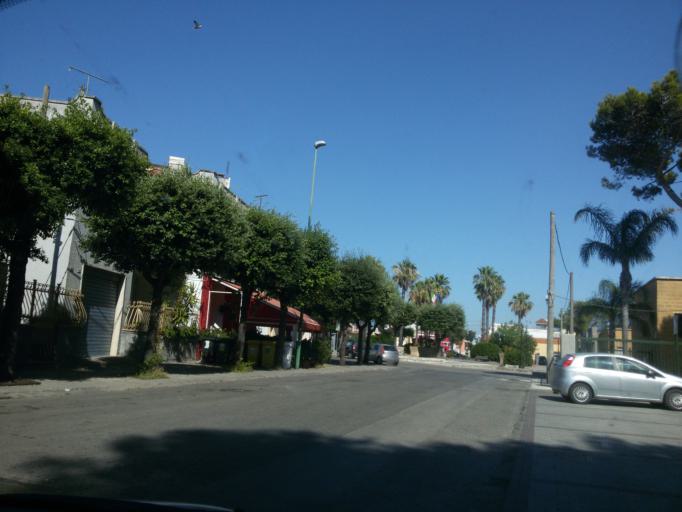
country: IT
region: Apulia
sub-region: Provincia di Brindisi
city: San Pancrazio Salentino
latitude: 40.4169
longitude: 17.8382
